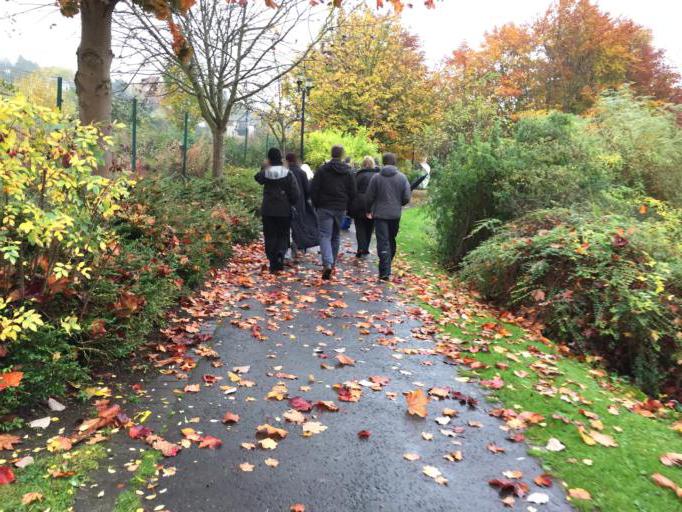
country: GB
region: Scotland
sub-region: Perth and Kinross
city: Perth
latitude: 56.3907
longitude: -3.4209
